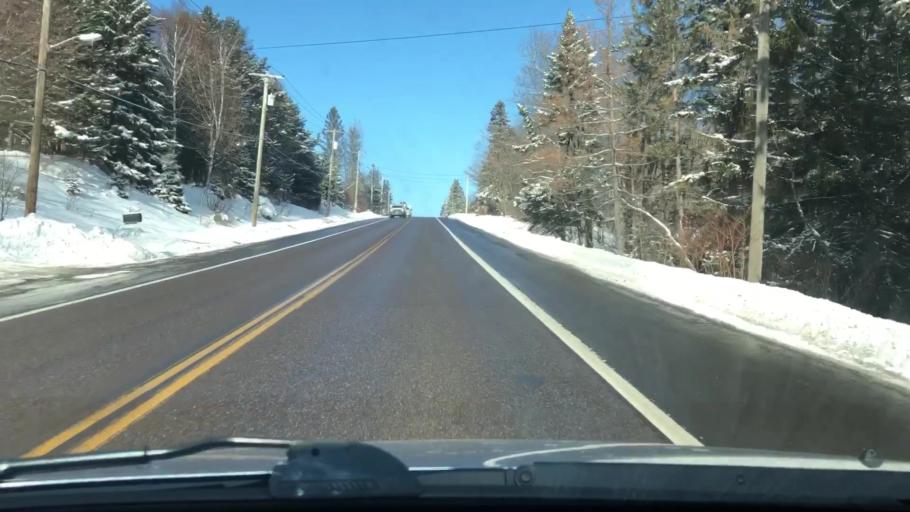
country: US
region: Minnesota
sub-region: Saint Louis County
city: Duluth
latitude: 46.8110
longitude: -92.1322
